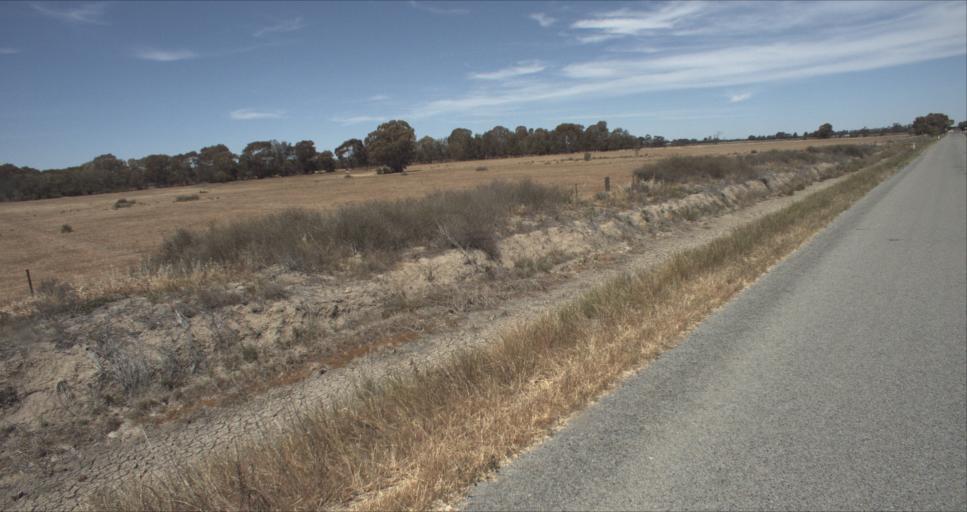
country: AU
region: New South Wales
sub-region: Leeton
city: Leeton
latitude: -34.5988
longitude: 146.4160
